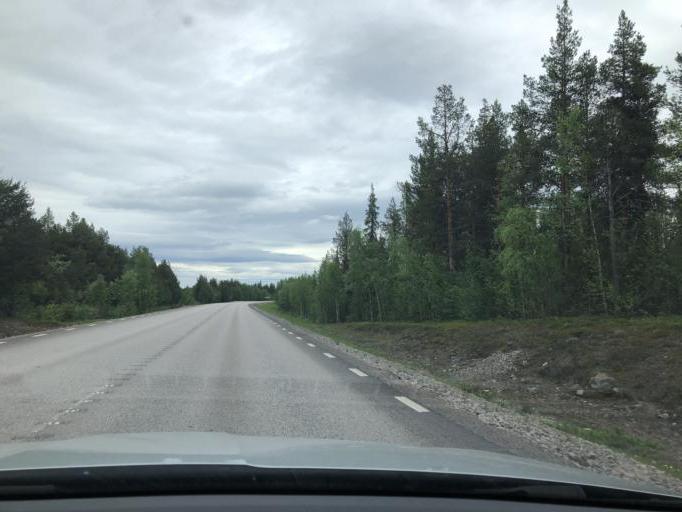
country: SE
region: Norrbotten
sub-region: Gallivare Kommun
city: Malmberget
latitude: 67.6486
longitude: 21.1603
